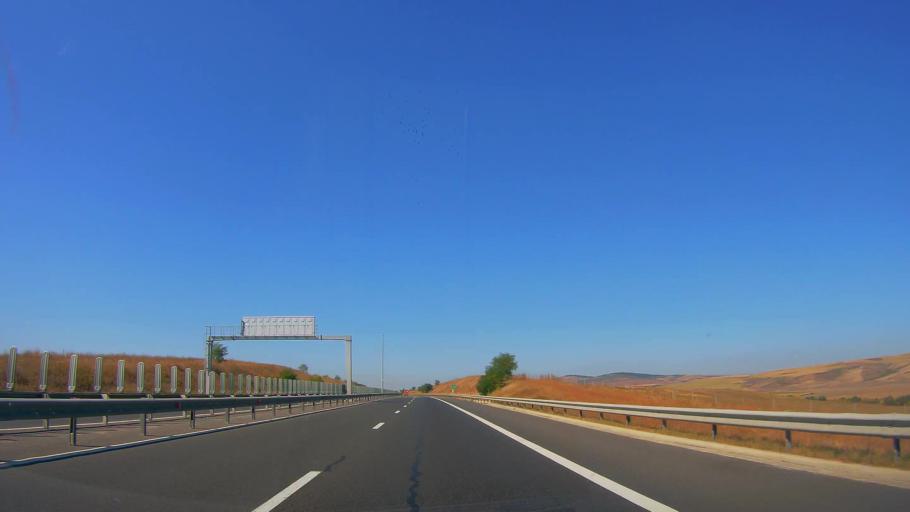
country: RO
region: Alba
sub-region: Comuna Cut
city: Cut
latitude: 45.9235
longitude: 23.6995
